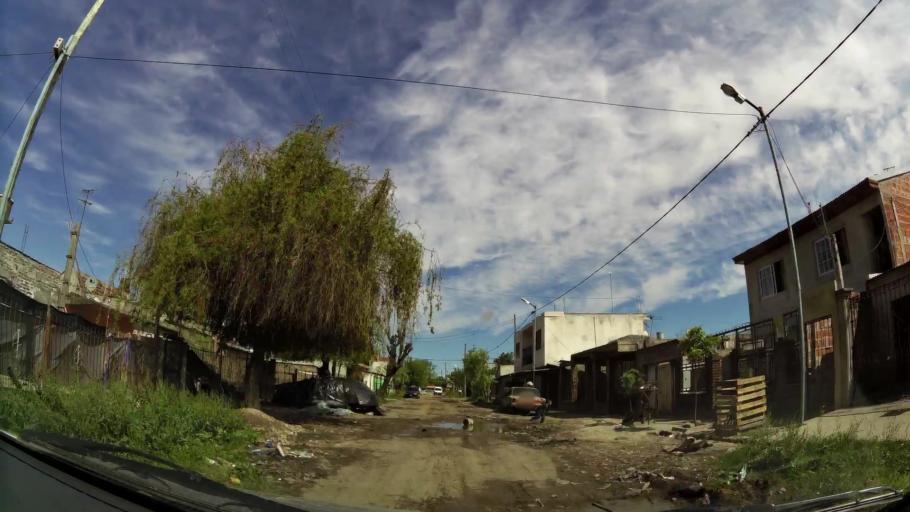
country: AR
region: Buenos Aires
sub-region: Partido de Quilmes
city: Quilmes
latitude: -34.7800
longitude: -58.2978
